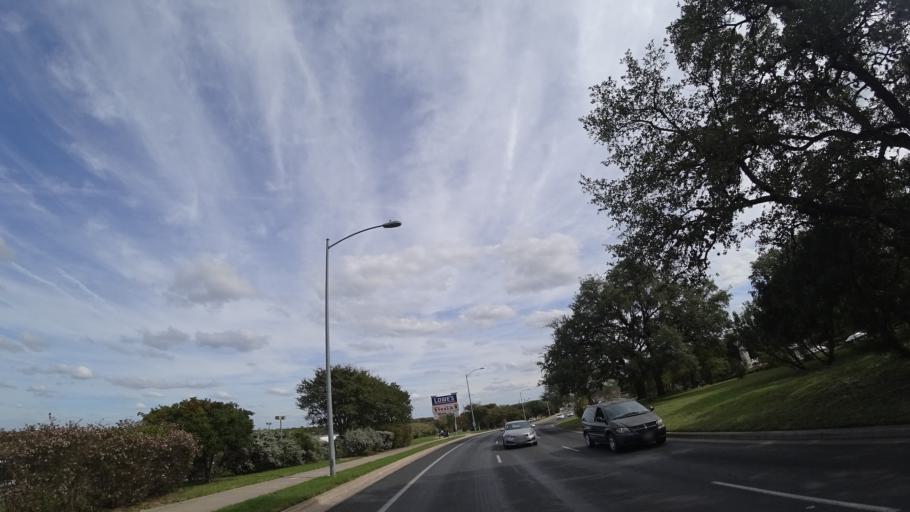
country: US
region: Texas
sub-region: Travis County
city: Onion Creek
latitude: 30.2005
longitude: -97.7667
